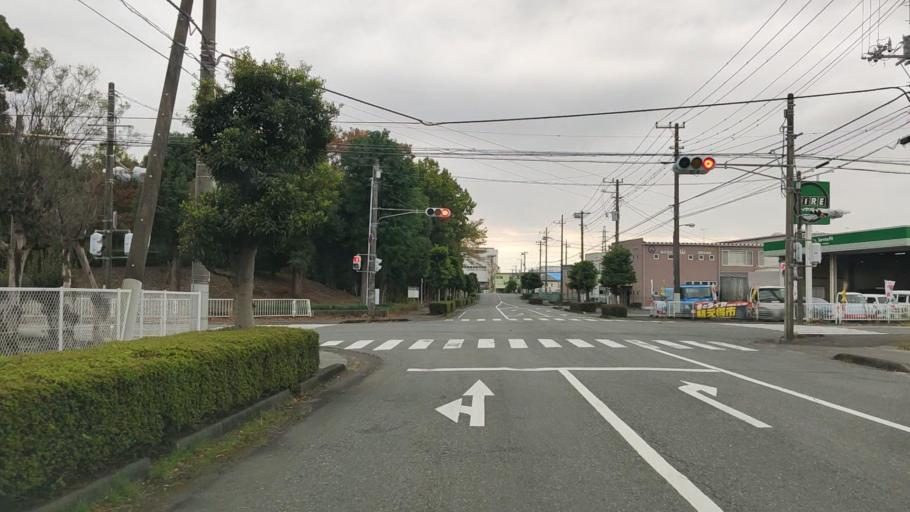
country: JP
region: Shizuoka
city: Fuji
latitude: 35.1522
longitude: 138.6882
